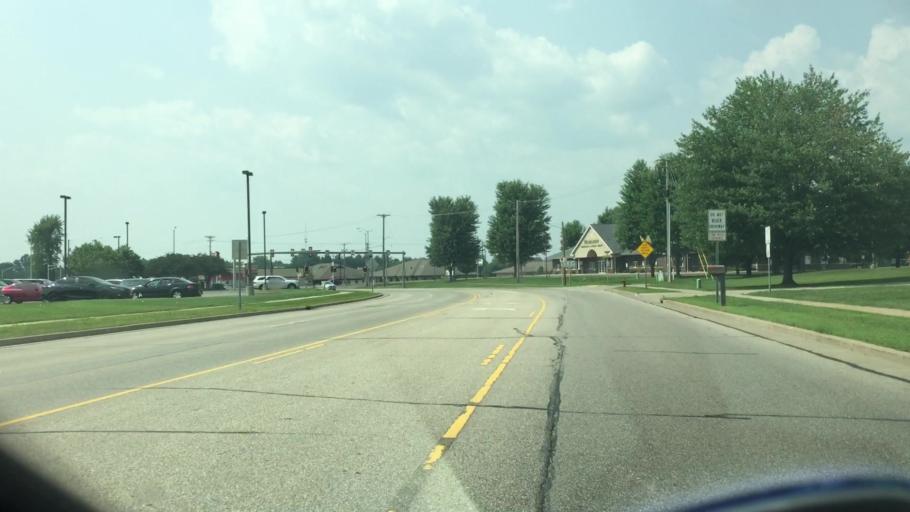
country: US
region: Wisconsin
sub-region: Eau Claire County
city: Altoona
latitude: 44.7705
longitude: -91.4572
